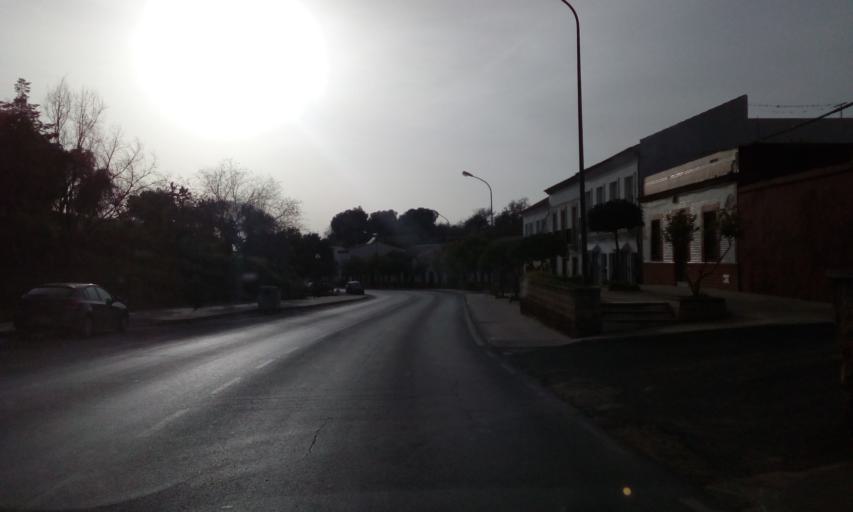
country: ES
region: Andalusia
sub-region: Provincia de Huelva
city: Niebla
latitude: 37.3611
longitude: -6.6820
